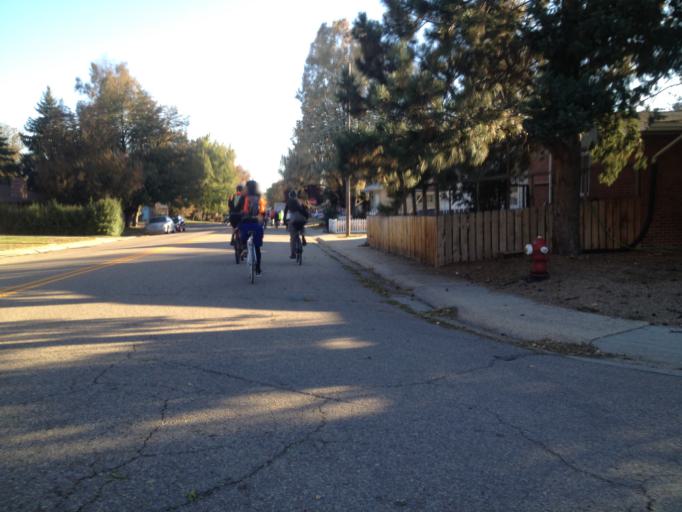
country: US
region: Colorado
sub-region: Boulder County
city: Longmont
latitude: 40.1820
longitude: -105.1144
